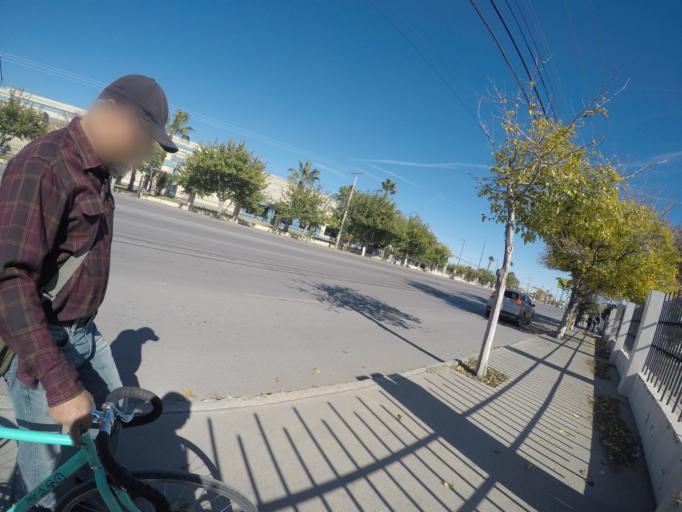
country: MX
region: Chihuahua
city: Ciudad Juarez
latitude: 31.7330
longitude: -106.4164
